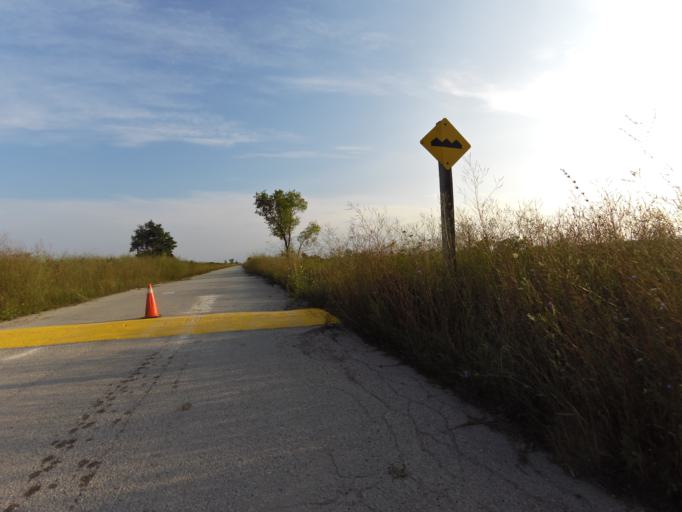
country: CA
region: Ontario
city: Toronto
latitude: 43.6260
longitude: -79.3237
